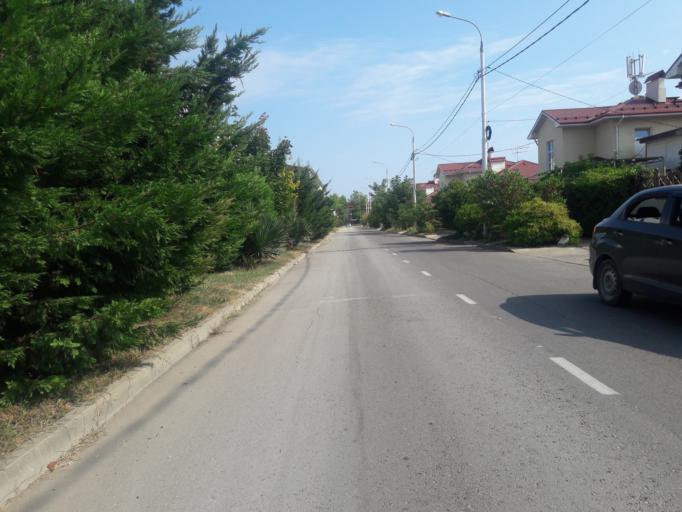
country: RU
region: Krasnodarskiy
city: Vysokoye
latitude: 43.3954
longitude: 40.0008
